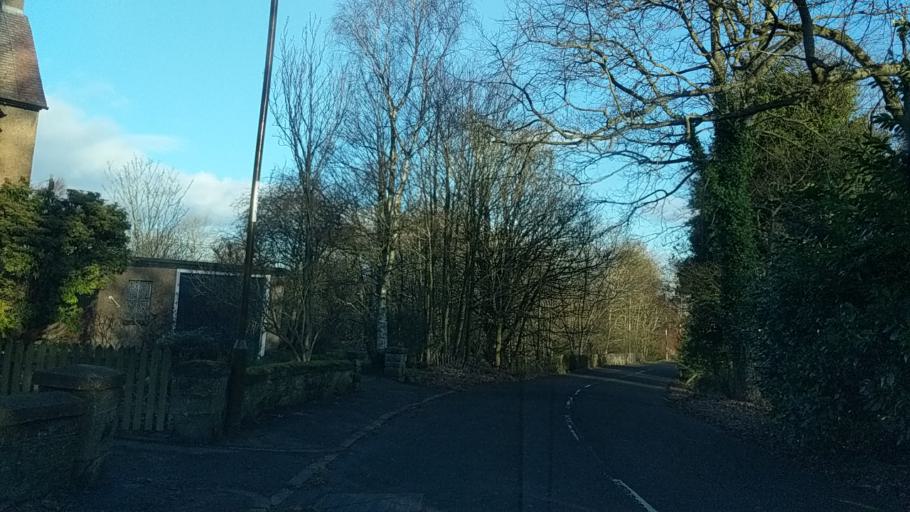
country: GB
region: Scotland
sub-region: West Lothian
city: Broxburn
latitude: 55.9775
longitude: -3.5252
